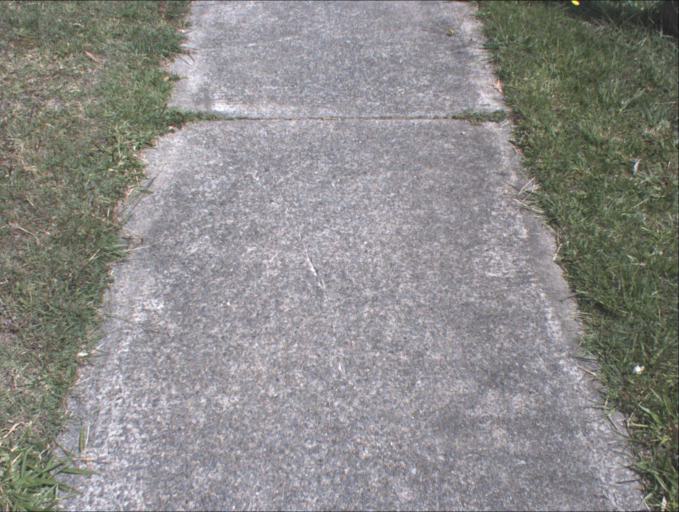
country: AU
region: Queensland
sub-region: Brisbane
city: Sunnybank Hills
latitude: -27.6672
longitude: 153.0391
